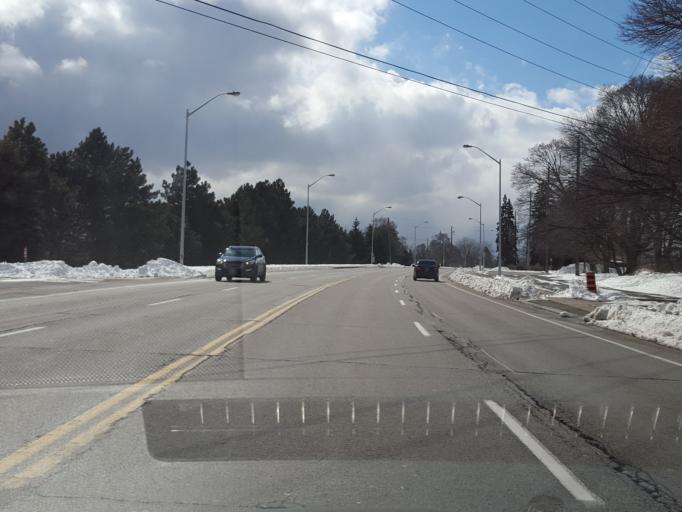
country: CA
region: Ontario
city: Hamilton
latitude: 43.2937
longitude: -79.8688
